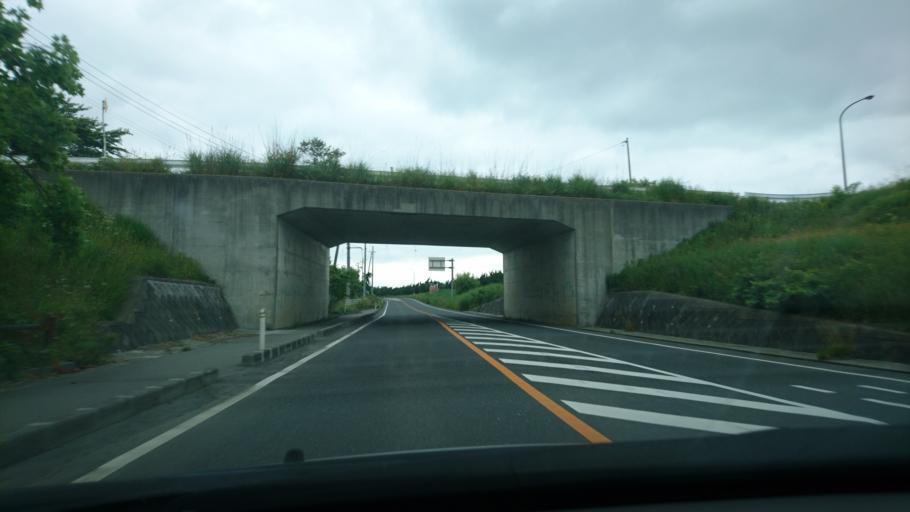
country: JP
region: Iwate
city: Ichinoseki
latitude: 38.7436
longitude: 141.1505
